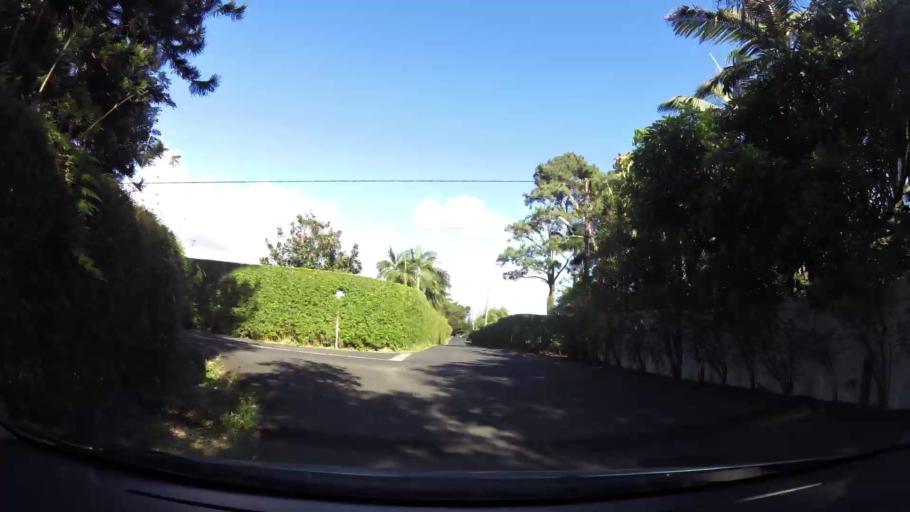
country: MU
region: Plaines Wilhems
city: Curepipe
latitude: -20.3090
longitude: 57.5019
